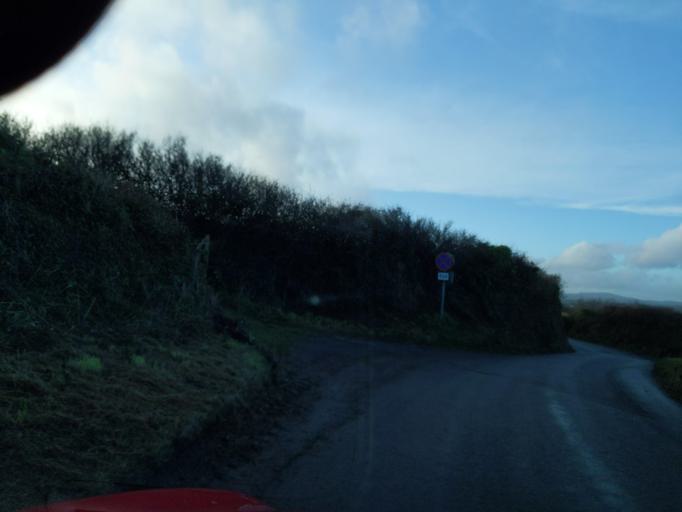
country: GB
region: England
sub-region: Cornwall
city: Fowey
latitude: 50.3292
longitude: -4.6205
